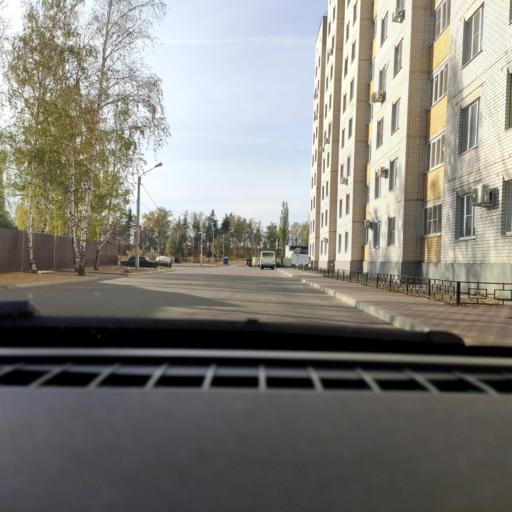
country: RU
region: Voronezj
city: Somovo
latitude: 51.7375
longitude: 39.3178
